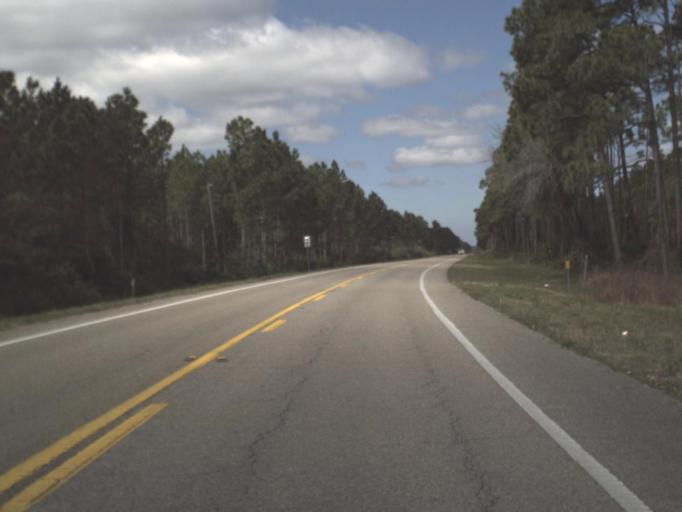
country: US
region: Florida
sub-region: Franklin County
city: Apalachicola
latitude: 29.7209
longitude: -85.1097
